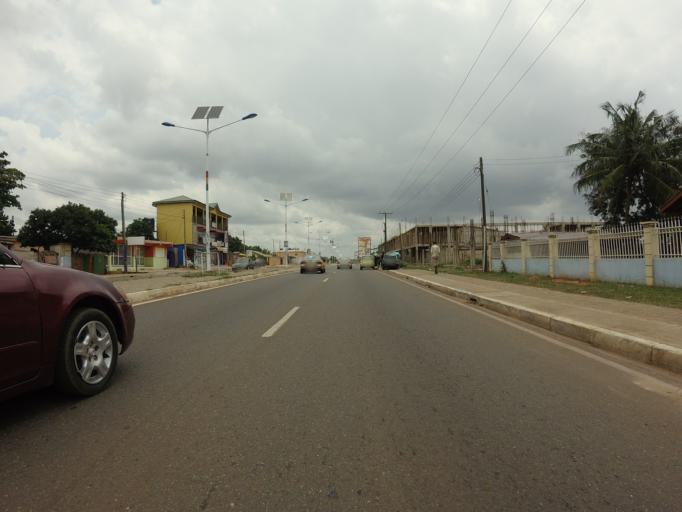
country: GH
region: Greater Accra
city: Medina Estates
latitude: 5.6631
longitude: -0.1514
